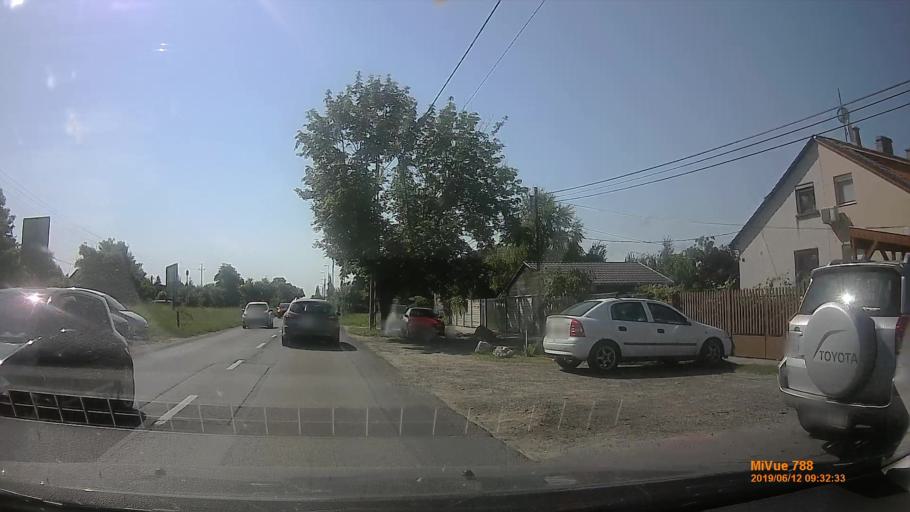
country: HU
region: Pest
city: Gyal
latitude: 47.3962
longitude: 19.1963
